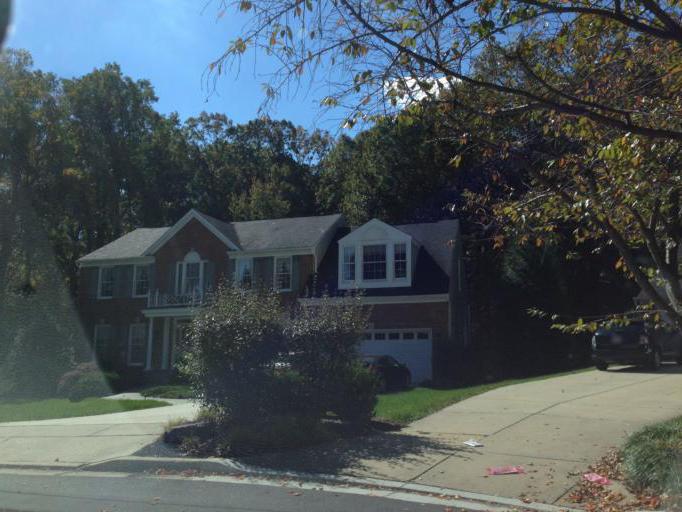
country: US
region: Maryland
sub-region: Howard County
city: Fulton
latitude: 39.1385
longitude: -76.9012
